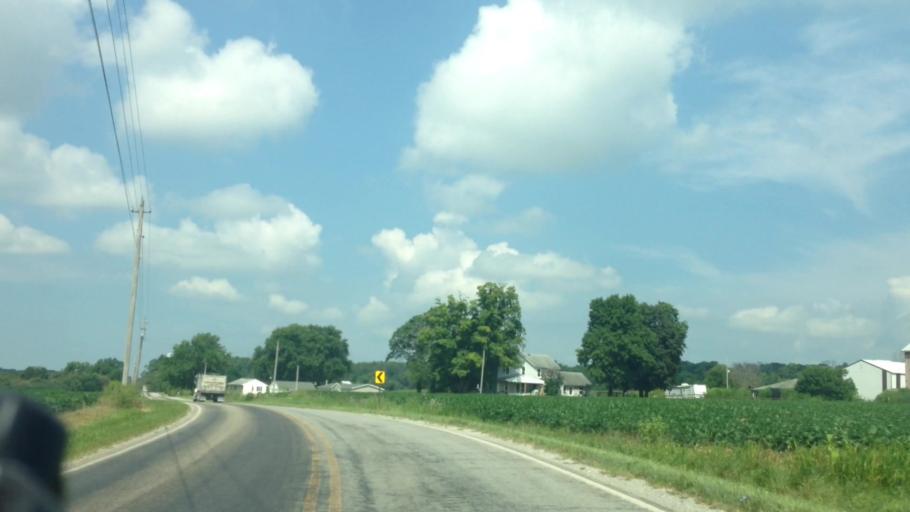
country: US
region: Ohio
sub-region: Wayne County
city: Dalton
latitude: 40.8680
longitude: -81.6868
